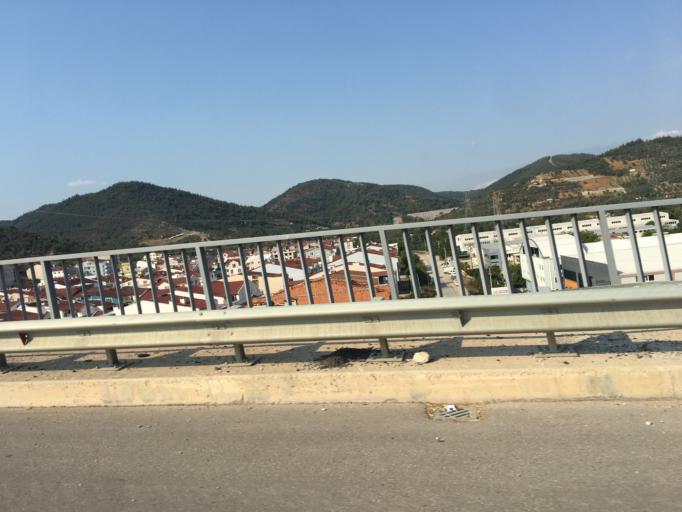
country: TR
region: Bursa
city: Demirtas
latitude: 40.2759
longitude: 29.1061
